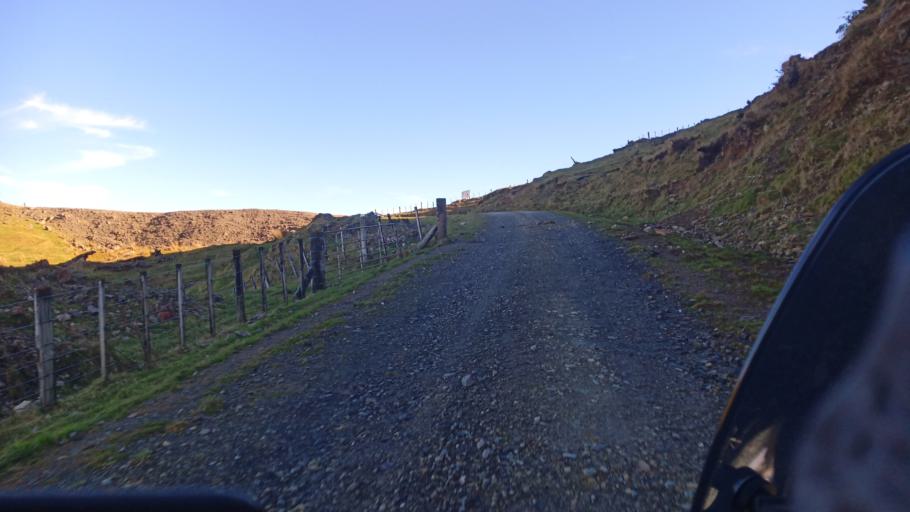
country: NZ
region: Gisborne
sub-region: Gisborne District
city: Gisborne
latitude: -38.1297
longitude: 177.8669
